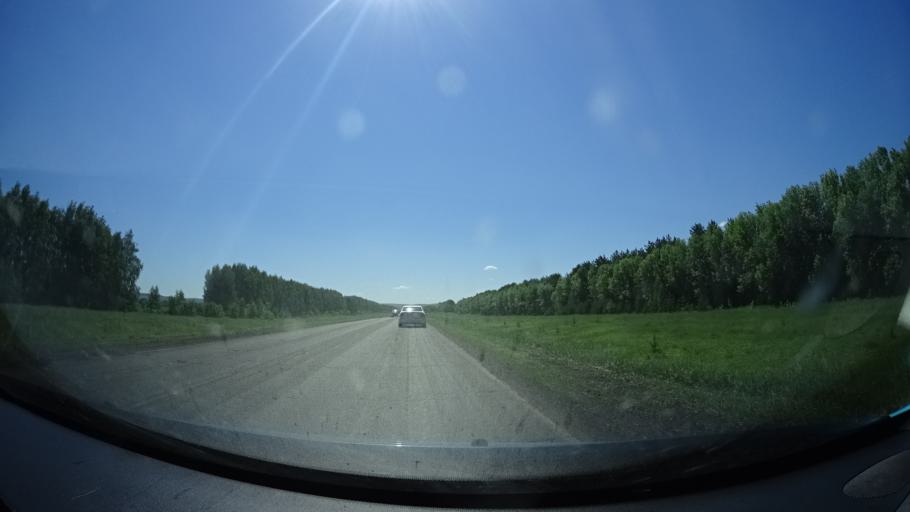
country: RU
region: Bashkortostan
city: Blagoveshchensk
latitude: 55.2342
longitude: 55.7785
